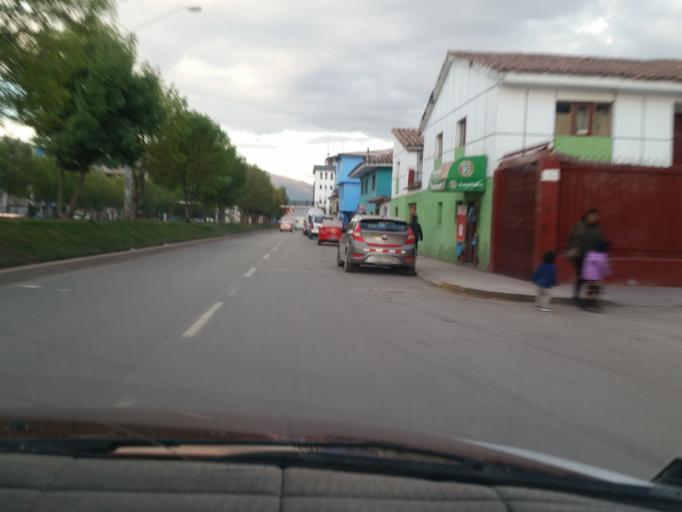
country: PE
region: Cusco
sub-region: Provincia de Cusco
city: Cusco
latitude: -13.5330
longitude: -71.9581
